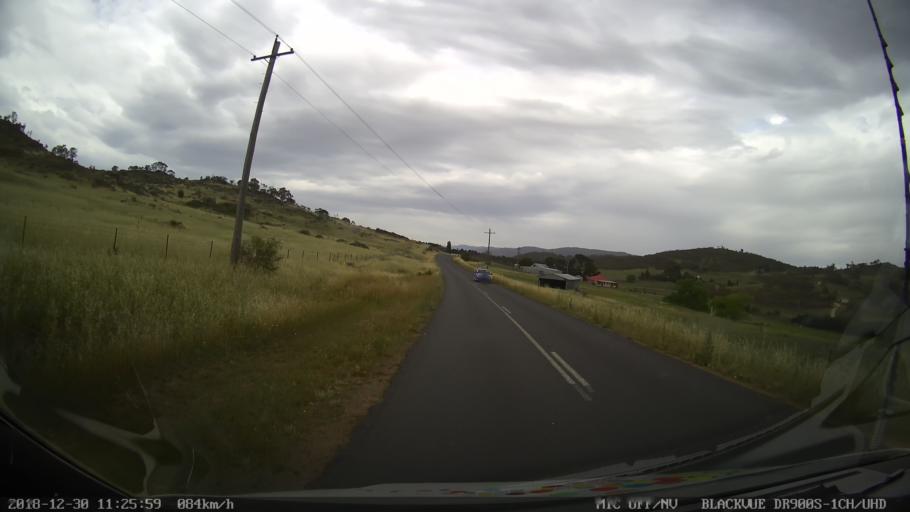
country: AU
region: New South Wales
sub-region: Snowy River
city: Jindabyne
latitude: -36.4685
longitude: 148.6402
